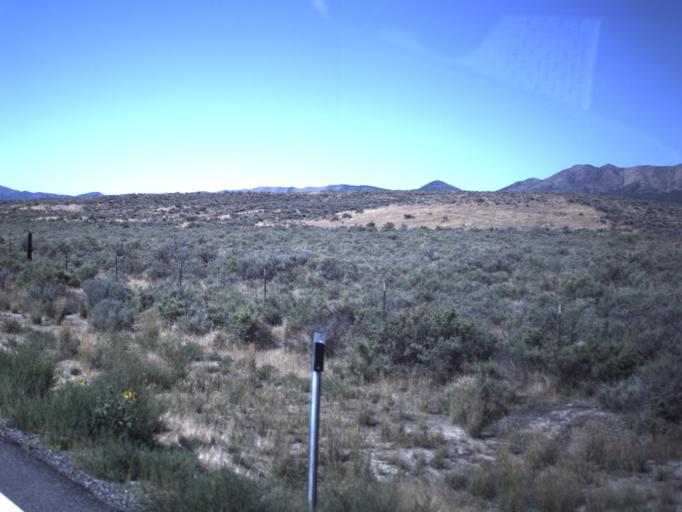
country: US
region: Utah
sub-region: Tooele County
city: Tooele
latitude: 40.1884
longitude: -112.4184
